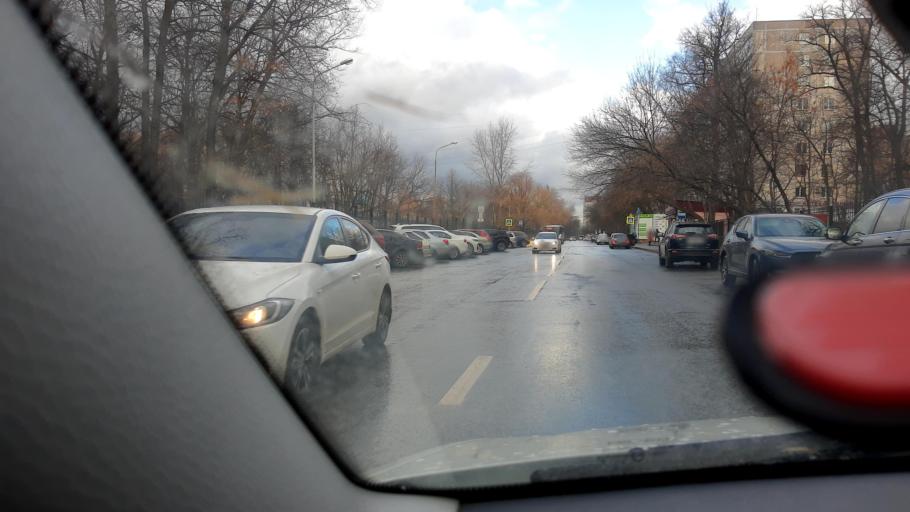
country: RU
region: Bashkortostan
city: Ufa
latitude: 54.7383
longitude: 56.0182
